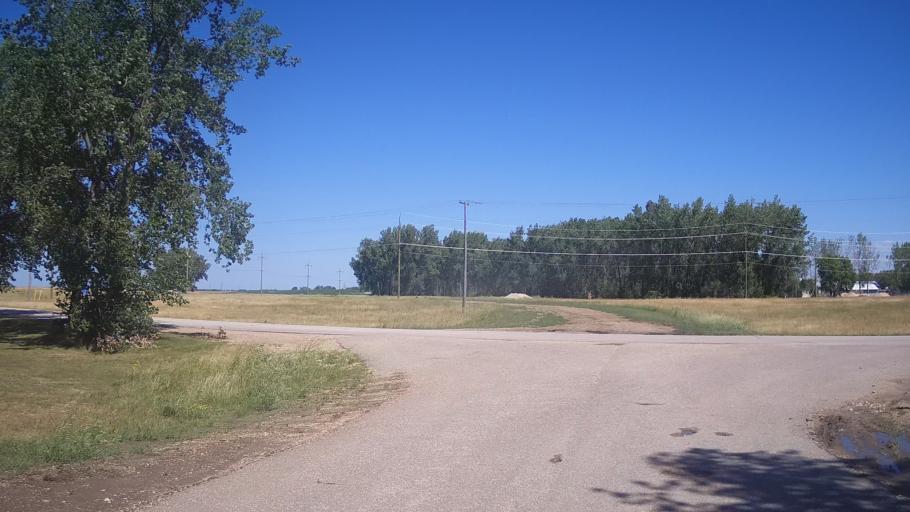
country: CA
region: Manitoba
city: Portage la Prairie
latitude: 49.9490
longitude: -98.3327
